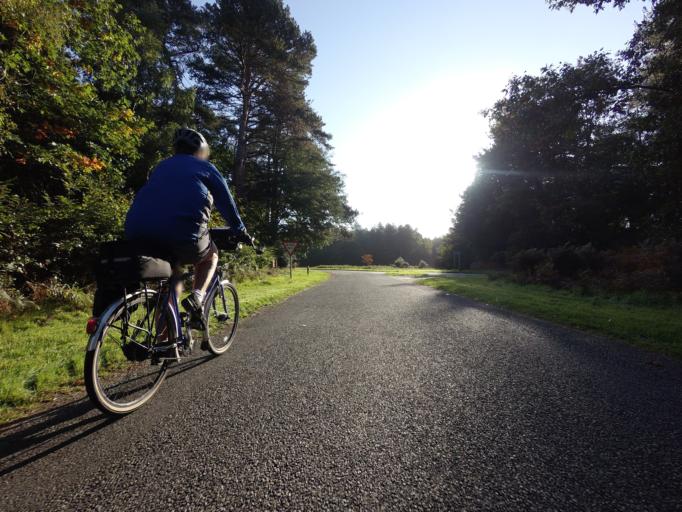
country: GB
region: England
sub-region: Norfolk
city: Dersingham
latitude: 52.8153
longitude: 0.5066
